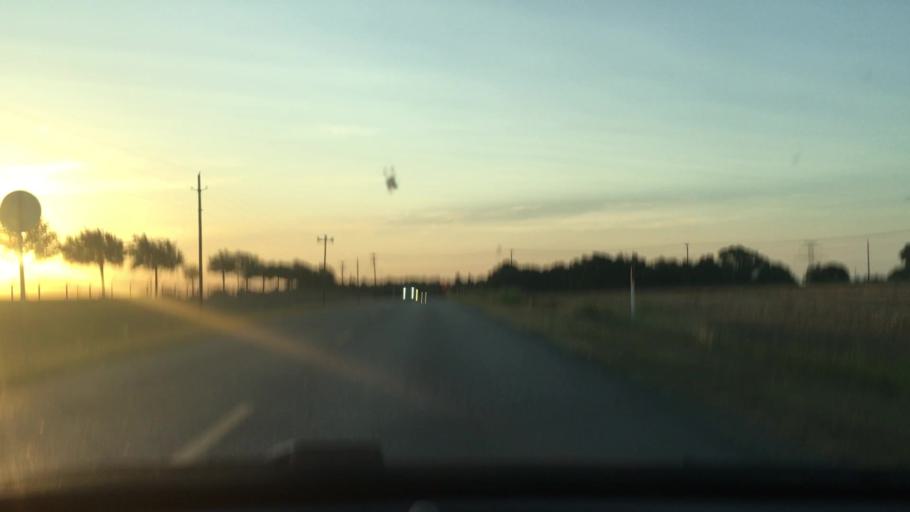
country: US
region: Texas
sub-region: Dallas County
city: Lancaster
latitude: 32.5608
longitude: -96.7731
